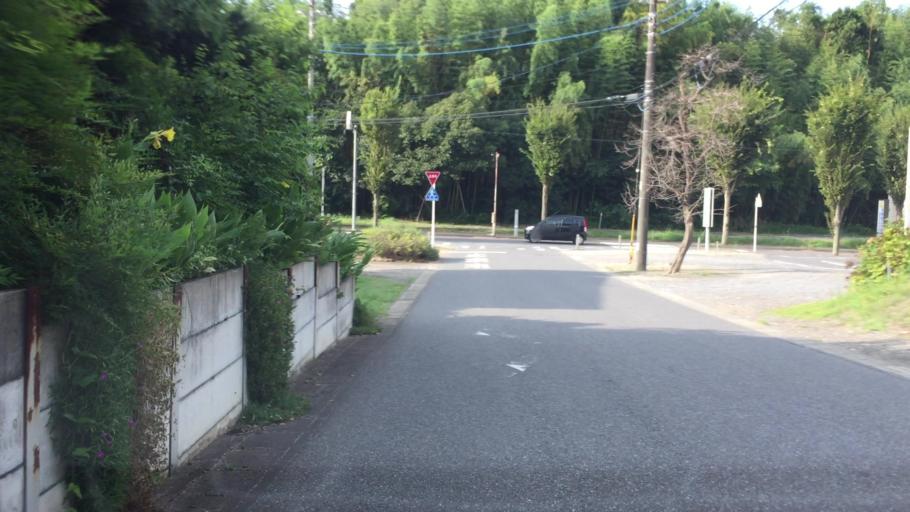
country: JP
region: Ibaraki
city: Toride
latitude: 35.8614
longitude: 140.1136
